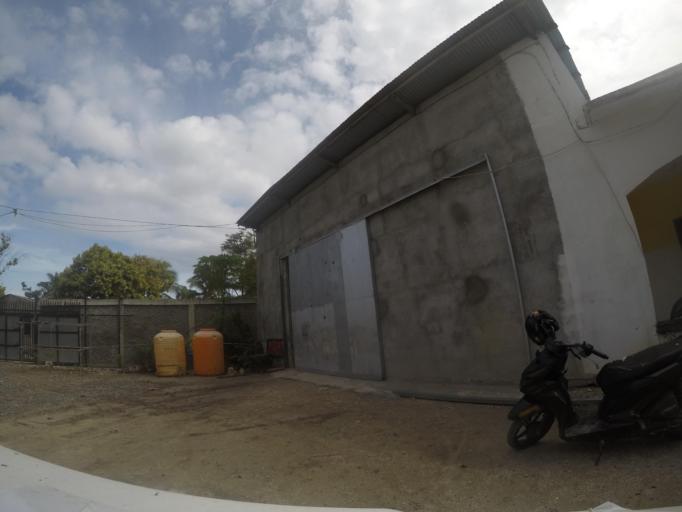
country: TL
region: Baucau
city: Baucau
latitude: -8.4676
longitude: 126.4585
